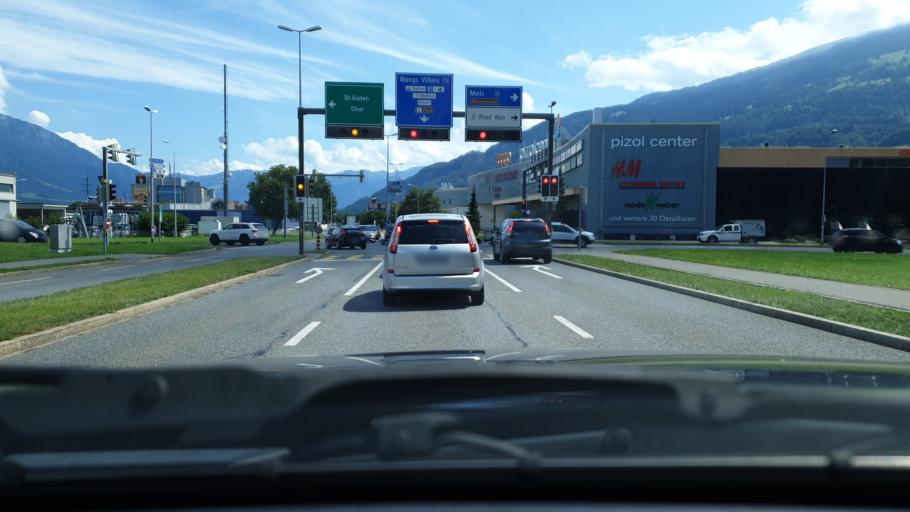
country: CH
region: Saint Gallen
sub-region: Wahlkreis Sarganserland
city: Sargans
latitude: 47.0420
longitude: 9.4342
